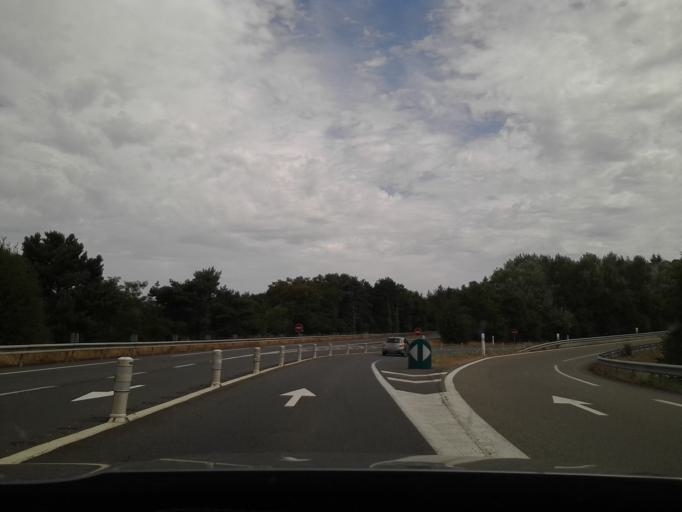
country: FR
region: Pays de la Loire
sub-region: Departement de la Sarthe
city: Rouillon
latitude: 48.0226
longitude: 0.1284
